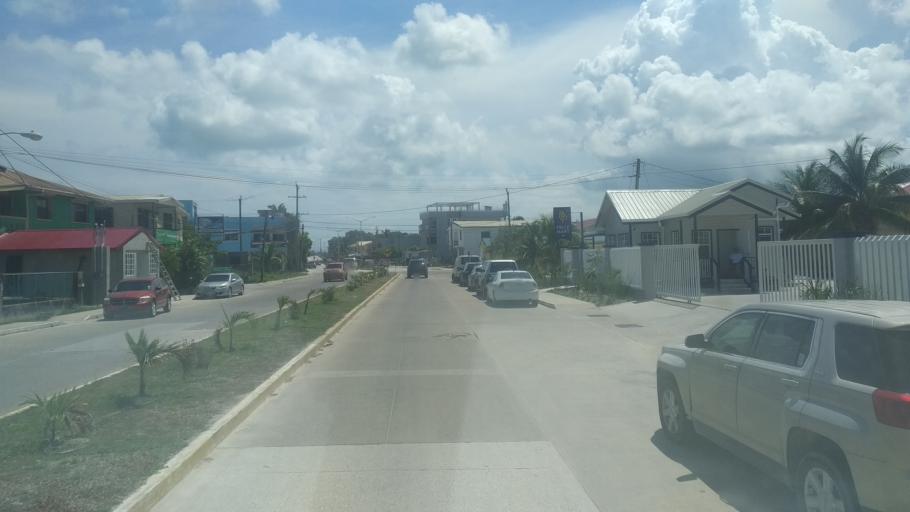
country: BZ
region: Belize
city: Belize City
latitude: 17.5114
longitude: -88.2214
